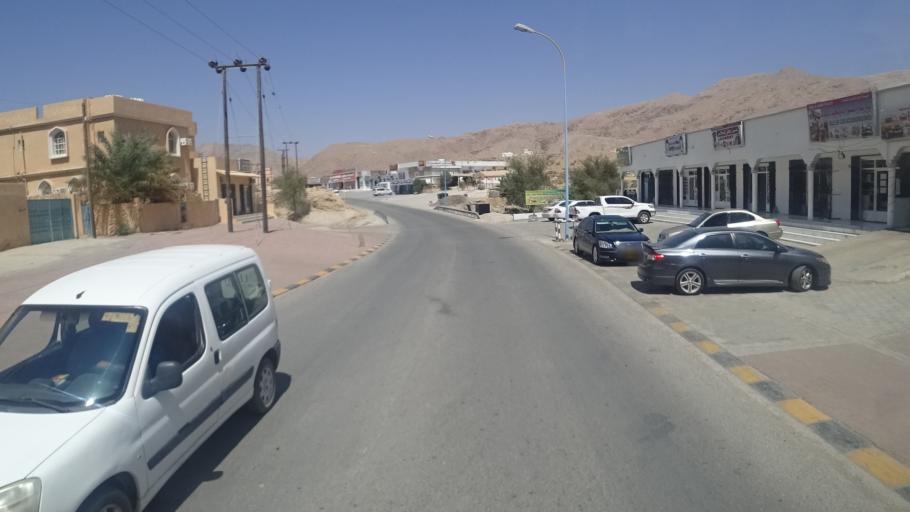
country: OM
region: Ash Sharqiyah
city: Badiyah
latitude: 22.5756
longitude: 59.0980
